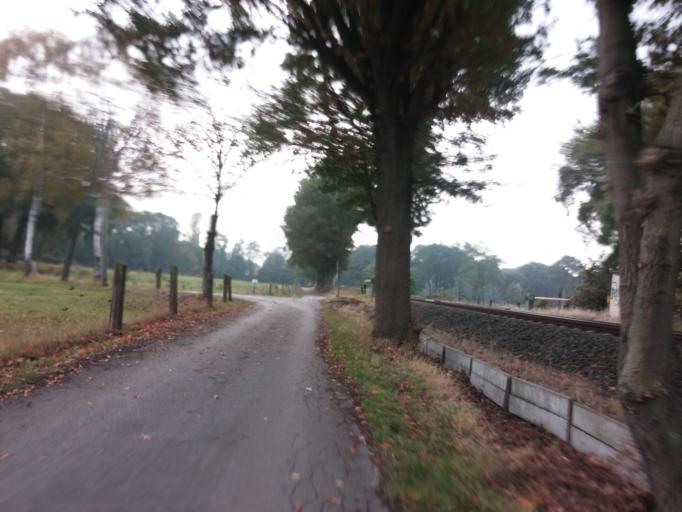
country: DE
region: North Rhine-Westphalia
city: Dorsten
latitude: 51.6385
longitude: 6.9695
